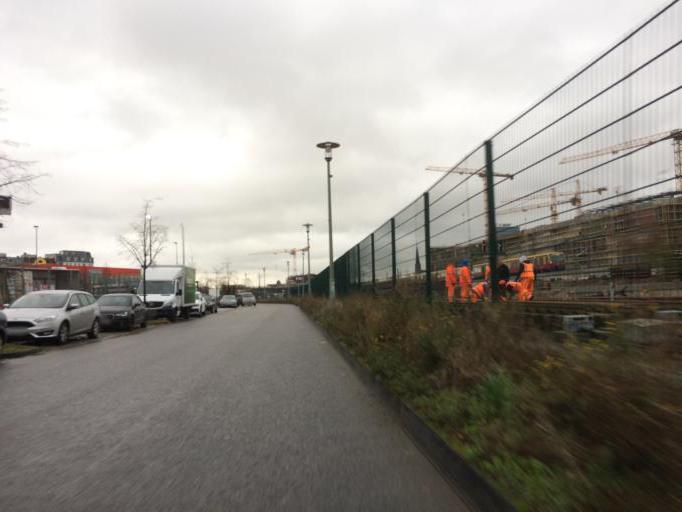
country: DE
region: Berlin
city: Friedrichshain Bezirk
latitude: 52.5080
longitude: 13.4442
